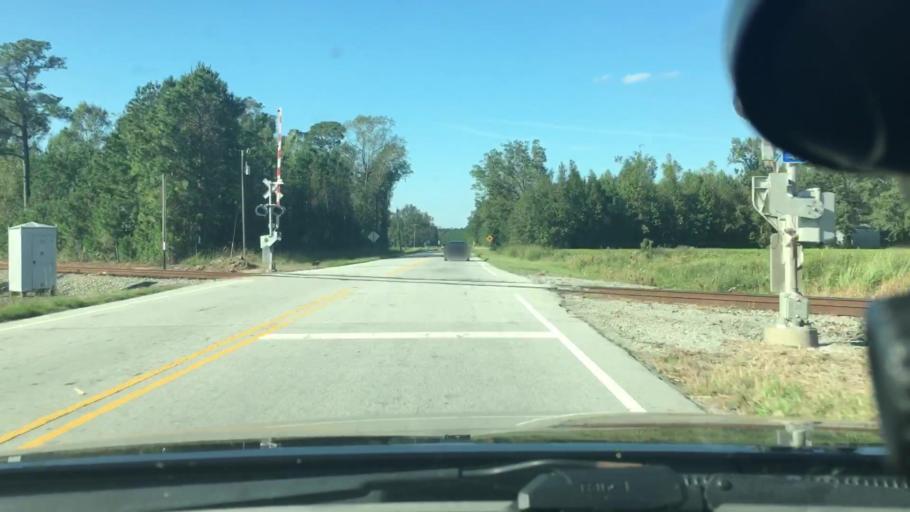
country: US
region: North Carolina
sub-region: Craven County
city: Vanceboro
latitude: 35.2919
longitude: -77.1296
